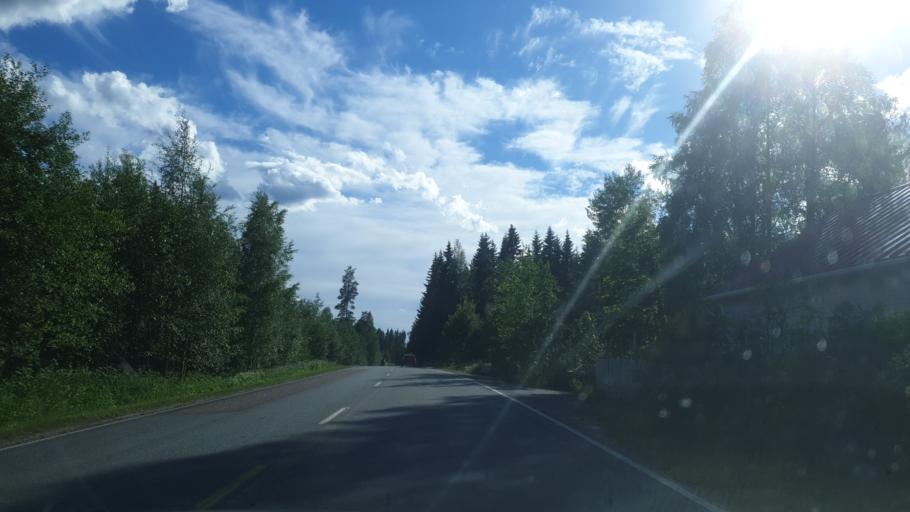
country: FI
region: Southern Savonia
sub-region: Mikkeli
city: Pertunmaa
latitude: 61.5221
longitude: 26.5036
